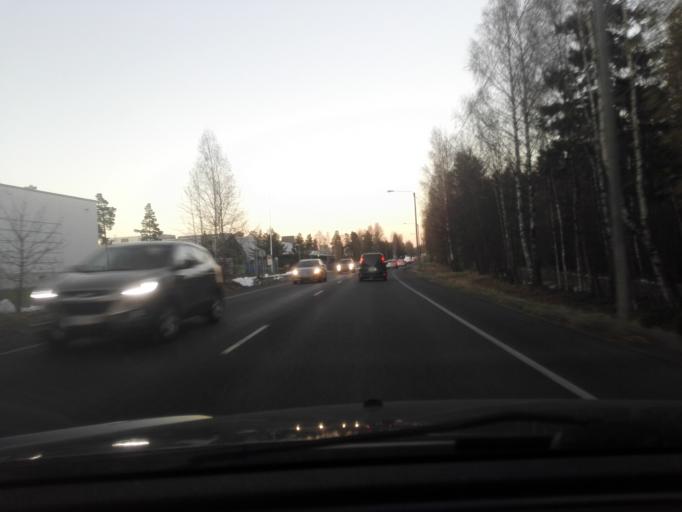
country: FI
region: Uusimaa
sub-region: Helsinki
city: Vantaa
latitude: 60.2925
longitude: 25.0997
